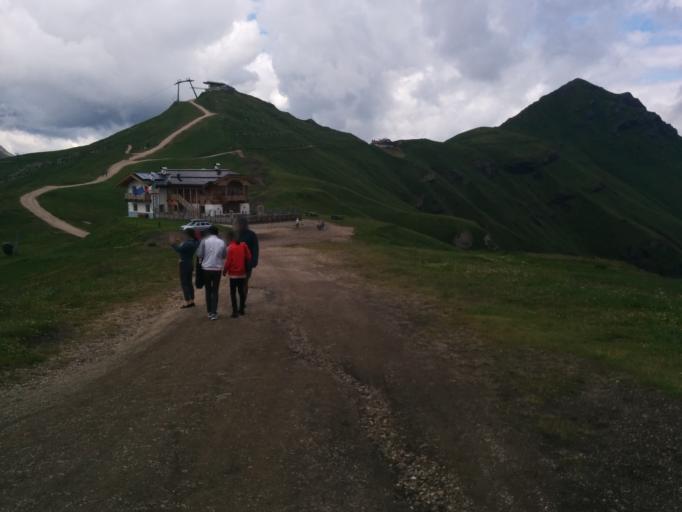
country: IT
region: Trentino-Alto Adige
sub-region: Provincia di Trento
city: Canazei
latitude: 46.4757
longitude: 11.8060
